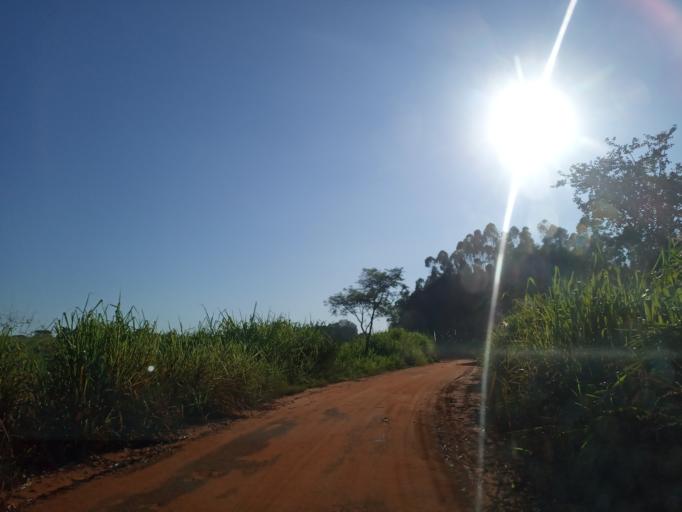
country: BR
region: Minas Gerais
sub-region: Ituiutaba
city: Ituiutaba
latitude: -18.9788
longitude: -49.5064
